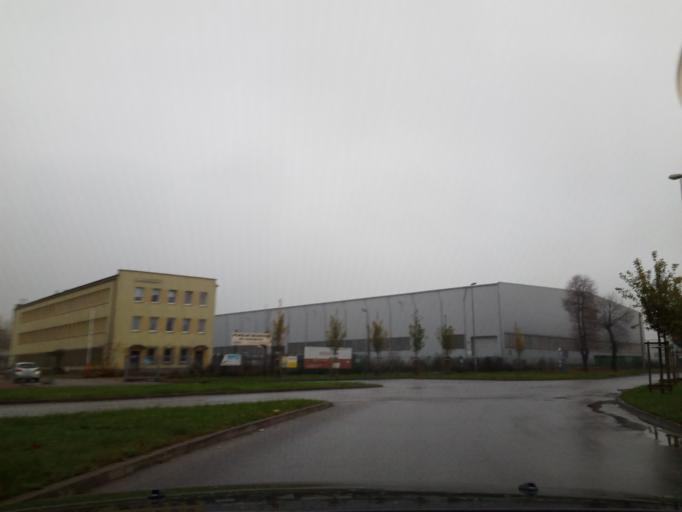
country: PL
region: Lesser Poland Voivodeship
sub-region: Powiat wielicki
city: Kokotow
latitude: 50.0878
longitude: 20.0655
